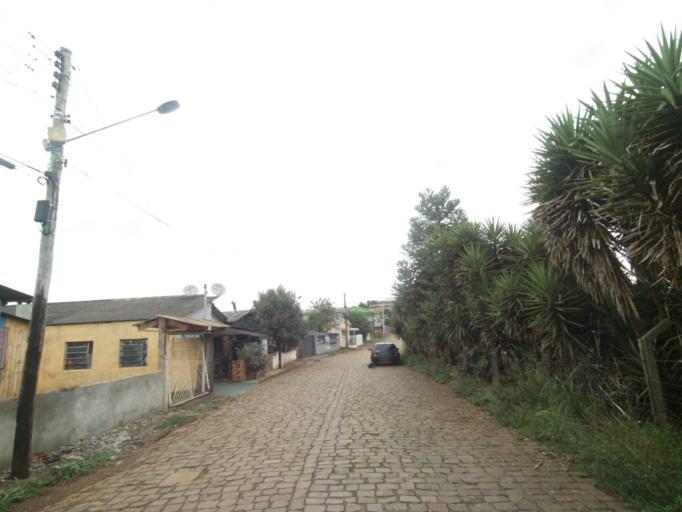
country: BR
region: Rio Grande do Sul
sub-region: Lagoa Vermelha
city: Lagoa Vermelha
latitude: -28.2222
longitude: -51.5240
